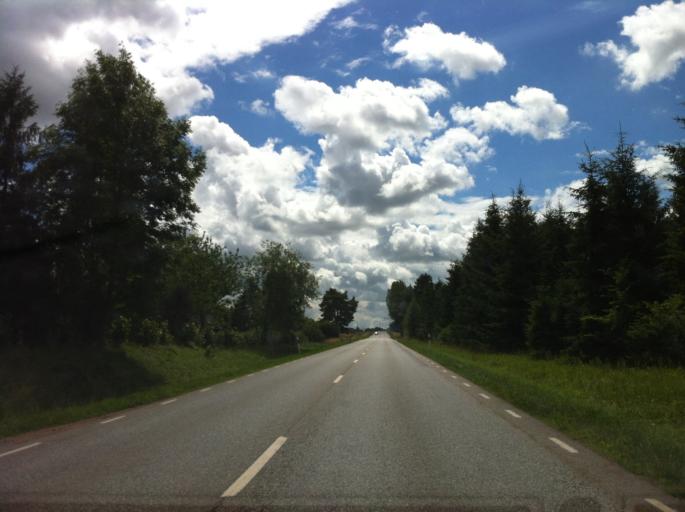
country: SE
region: Skane
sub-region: Svedala Kommun
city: Klagerup
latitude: 55.5774
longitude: 13.2527
